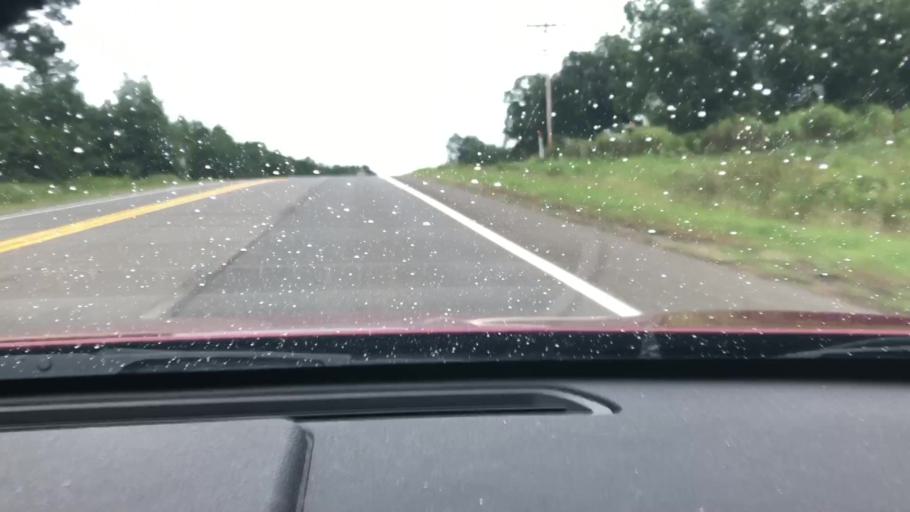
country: US
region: Arkansas
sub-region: Columbia County
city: Waldo
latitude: 33.3510
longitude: -93.3696
